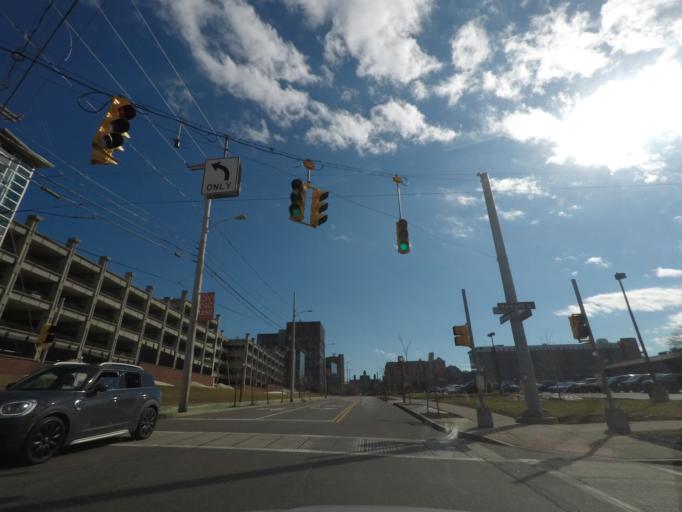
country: US
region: New York
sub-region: Onondaga County
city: Syracuse
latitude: 43.0442
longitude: -76.1345
